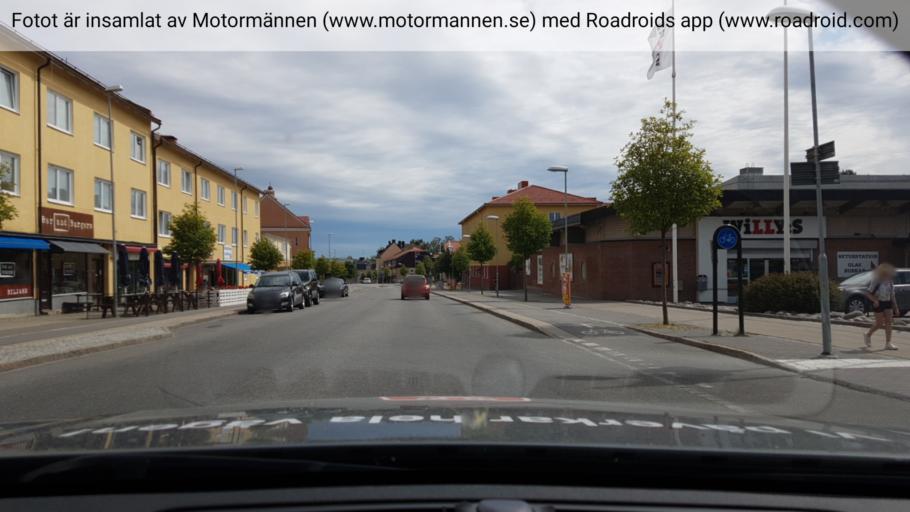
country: SE
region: Stockholm
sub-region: Nynashamns Kommun
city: Nynashamn
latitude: 58.9133
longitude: 17.9476
